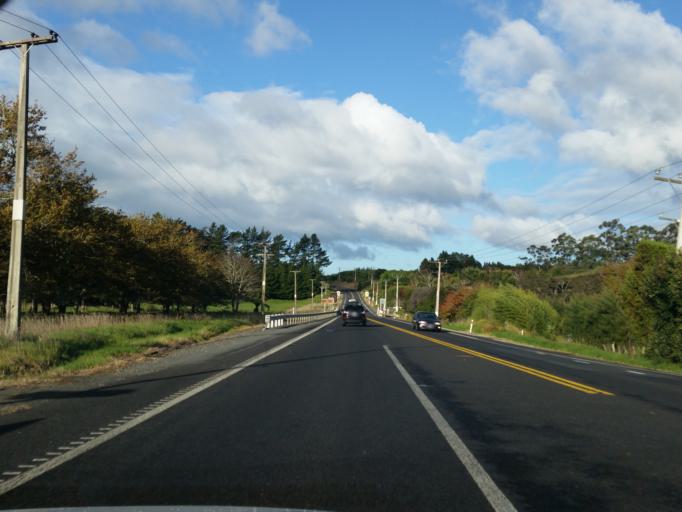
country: NZ
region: Bay of Plenty
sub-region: Western Bay of Plenty District
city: Katikati
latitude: -37.6007
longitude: 175.9176
